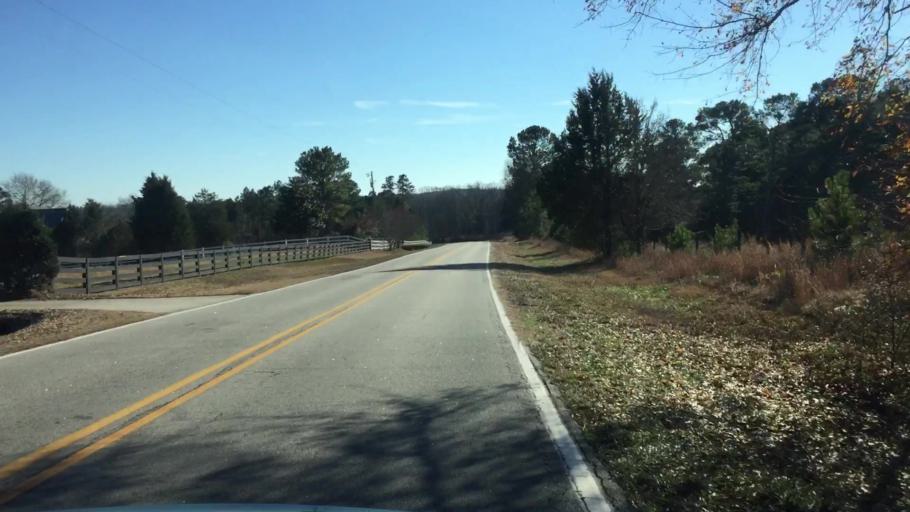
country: US
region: Georgia
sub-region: Newton County
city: Oakwood
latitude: 33.4944
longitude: -84.0471
